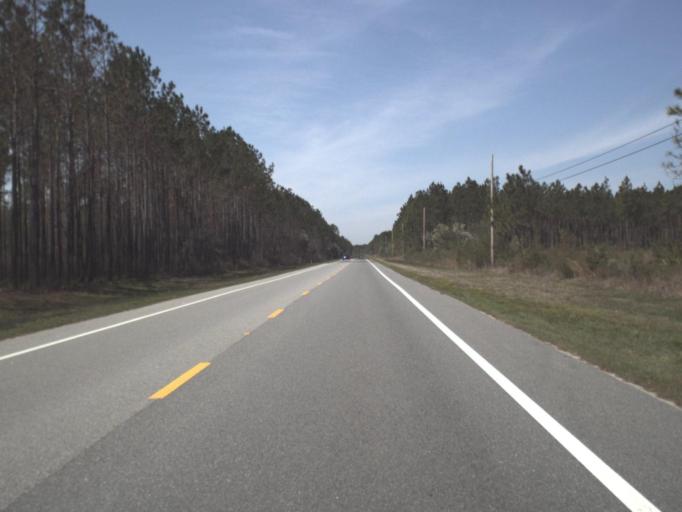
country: US
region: Florida
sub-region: Bay County
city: Lynn Haven
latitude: 30.3254
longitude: -85.7020
